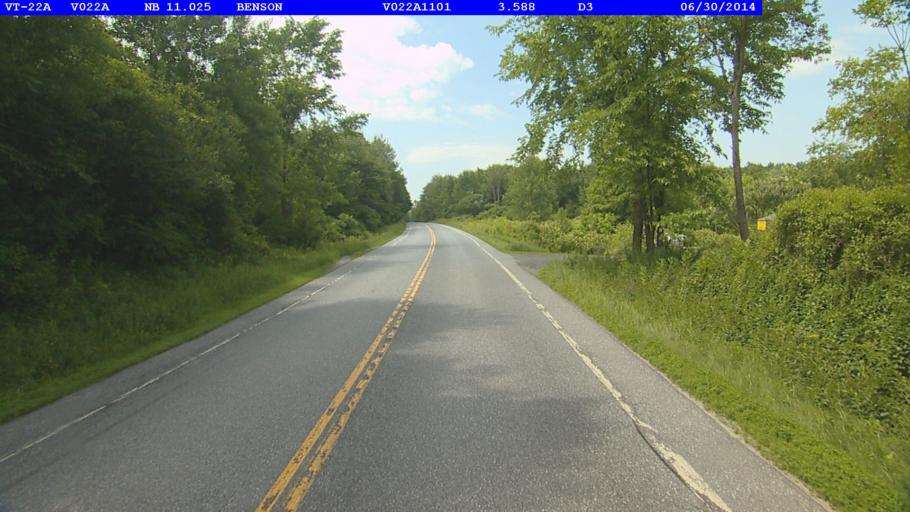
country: US
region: Vermont
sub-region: Rutland County
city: Fair Haven
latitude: 43.7200
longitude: -73.2991
